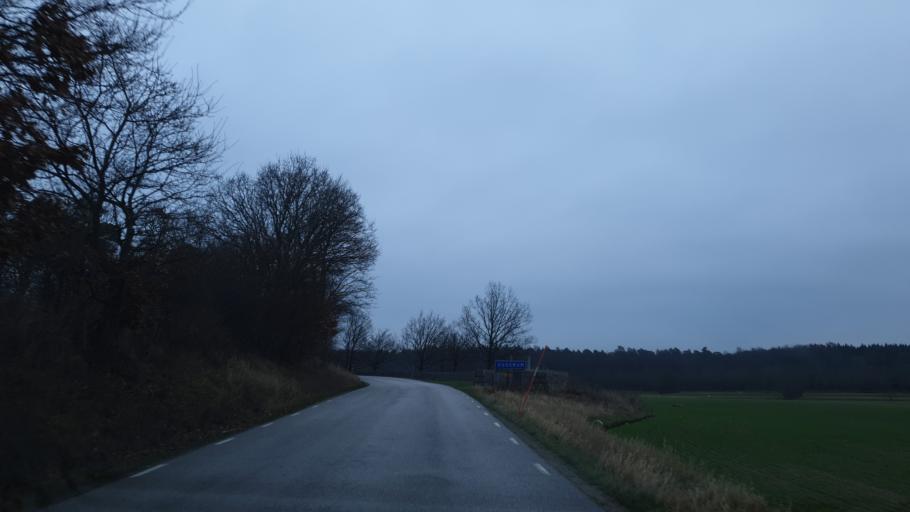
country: SE
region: Blekinge
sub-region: Karlskrona Kommun
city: Rodeby
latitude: 56.2125
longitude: 15.6766
